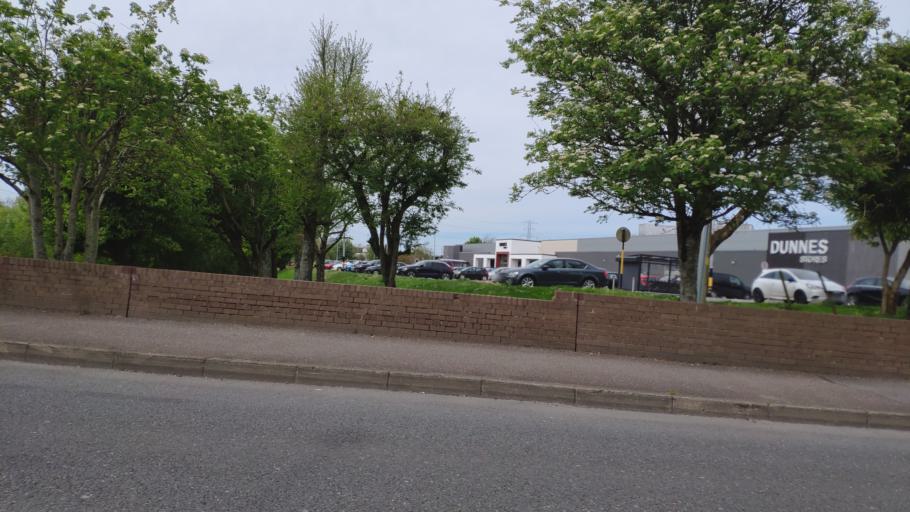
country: IE
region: Munster
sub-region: County Cork
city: Cork
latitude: 51.9158
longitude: -8.4468
